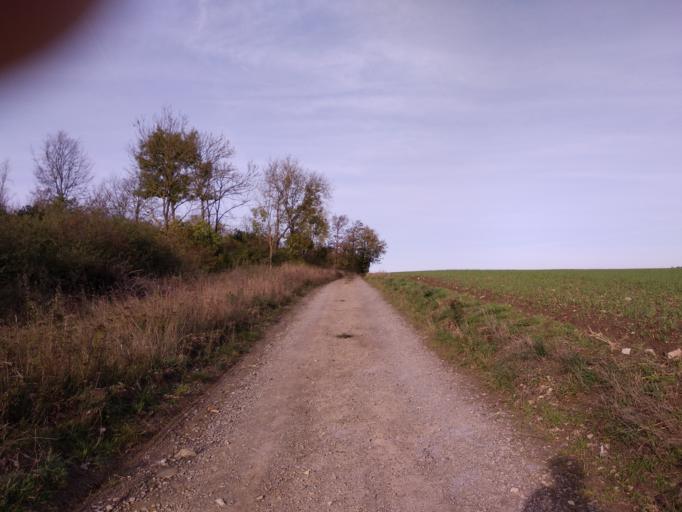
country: DE
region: North Rhine-Westphalia
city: Beverungen
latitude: 51.6787
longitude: 9.3602
